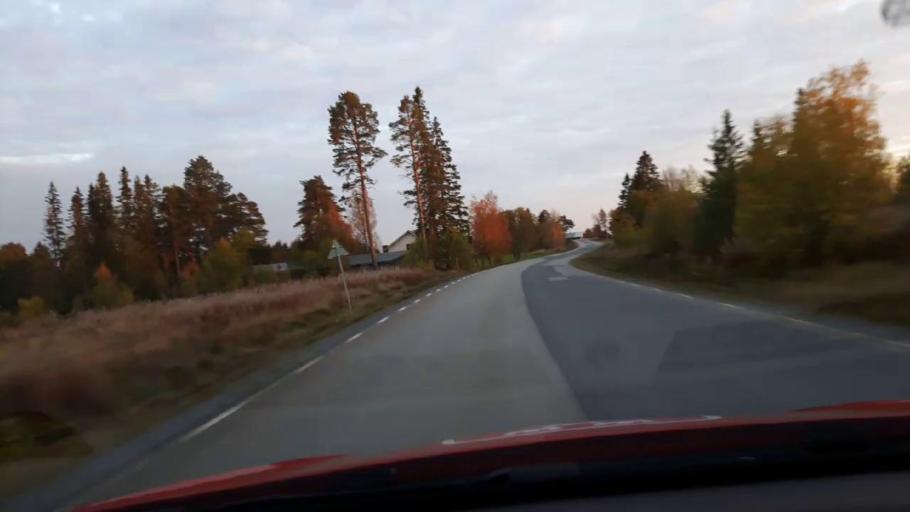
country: SE
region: Jaemtland
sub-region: OEstersunds Kommun
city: Ostersund
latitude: 63.2609
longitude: 14.6087
